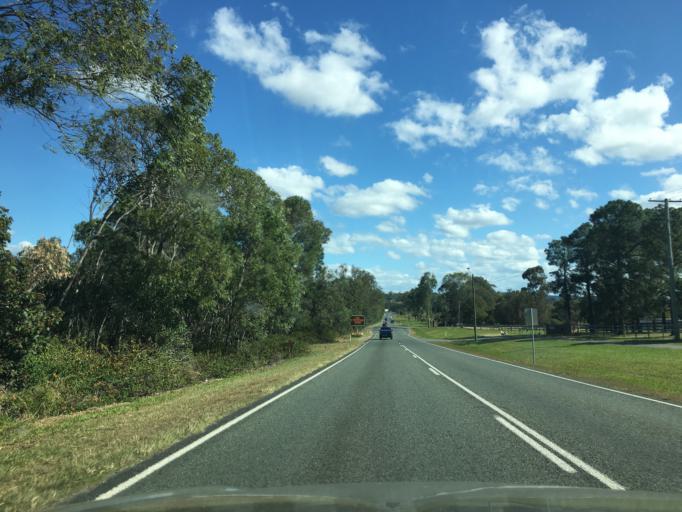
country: AU
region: Queensland
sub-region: Logan
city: Logan Reserve
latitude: -27.7434
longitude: 153.1268
